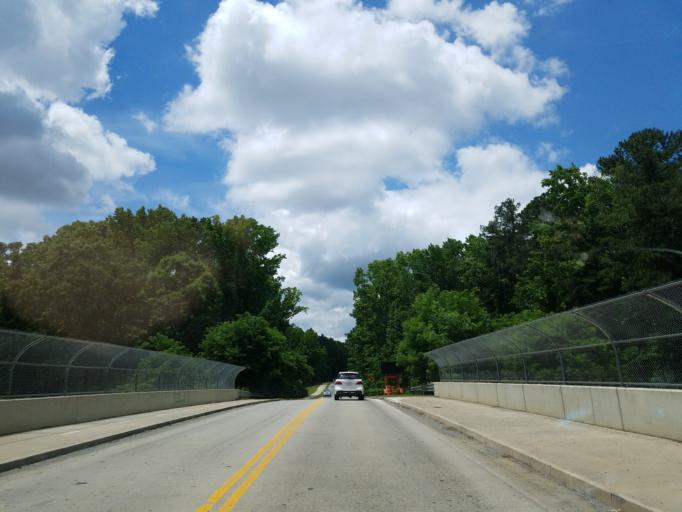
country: US
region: Georgia
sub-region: Cobb County
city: Marietta
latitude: 33.9858
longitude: -84.5822
